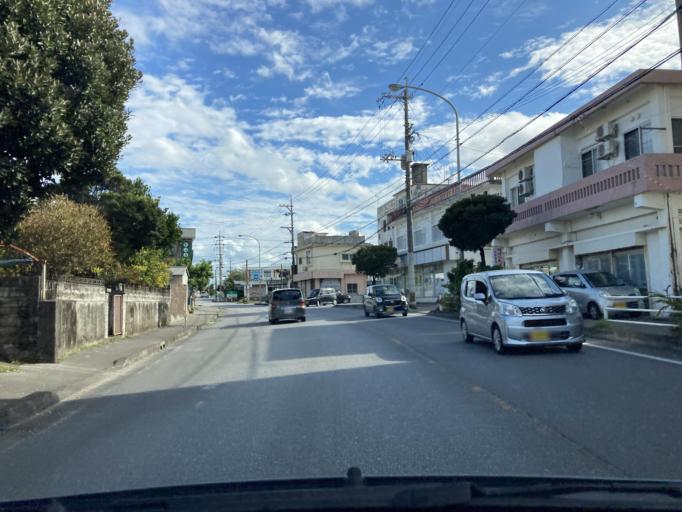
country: JP
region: Okinawa
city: Ishikawa
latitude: 26.4183
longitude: 127.8183
